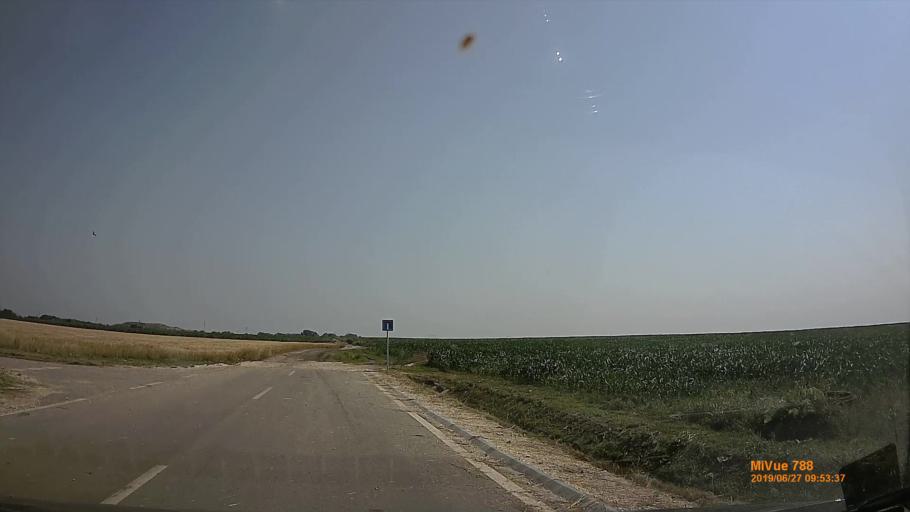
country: HU
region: Pest
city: Cegledbercel
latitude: 47.2167
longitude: 19.7362
